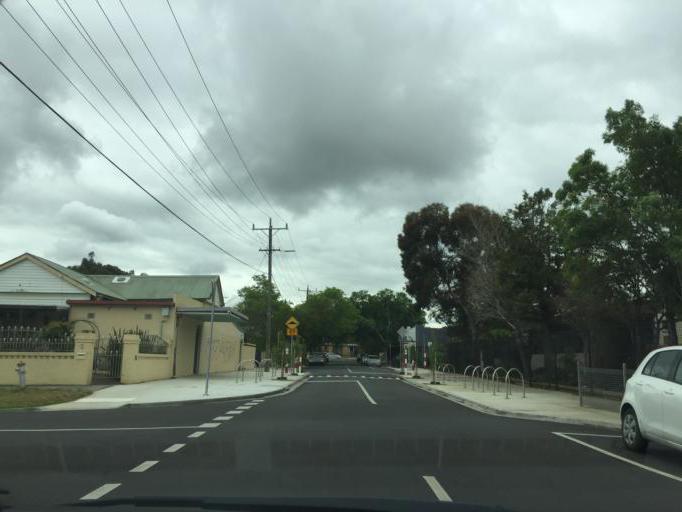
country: AU
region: Victoria
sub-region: Maribyrnong
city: West Footscray
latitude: -37.7946
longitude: 144.8750
